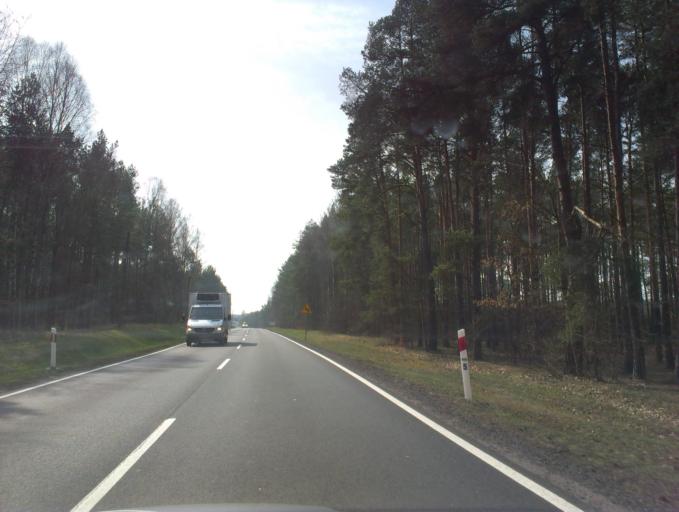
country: PL
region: Greater Poland Voivodeship
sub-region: Powiat zlotowski
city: Tarnowka
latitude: 53.3147
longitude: 16.7942
